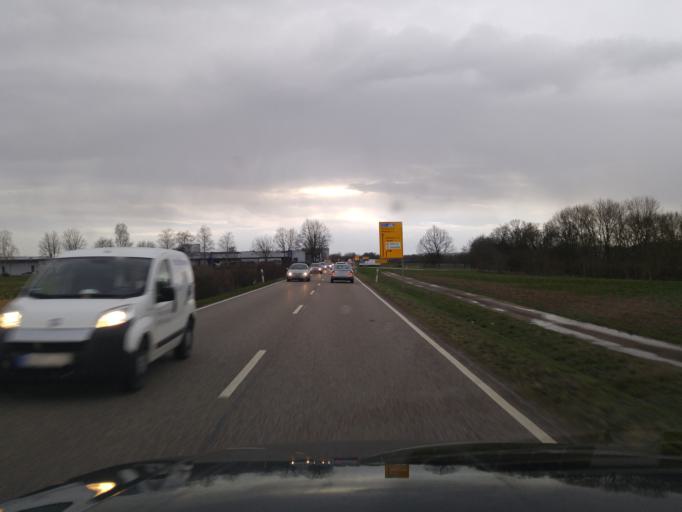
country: DE
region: Baden-Wuerttemberg
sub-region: Regierungsbezirk Stuttgart
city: Neuenstadt am Kocher
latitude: 49.2336
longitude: 9.3618
